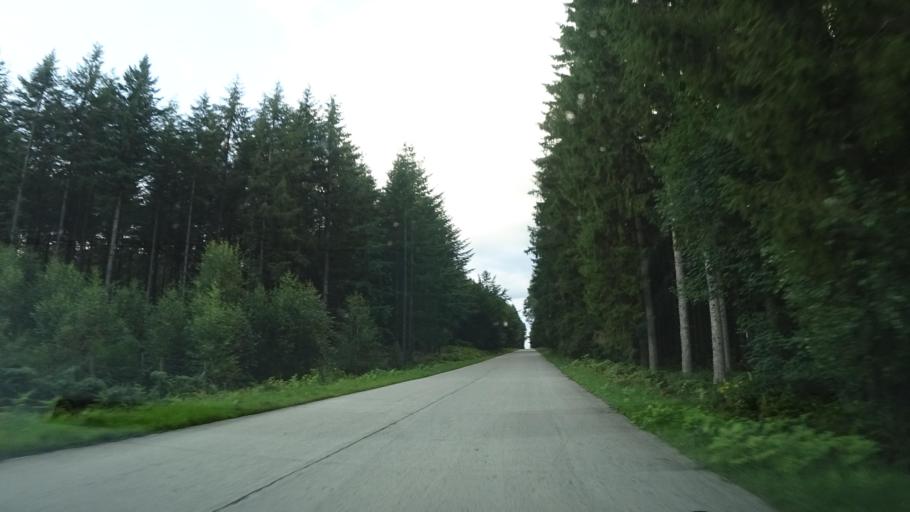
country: BE
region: Wallonia
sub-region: Province du Luxembourg
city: Herbeumont
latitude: 49.7967
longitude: 5.2565
